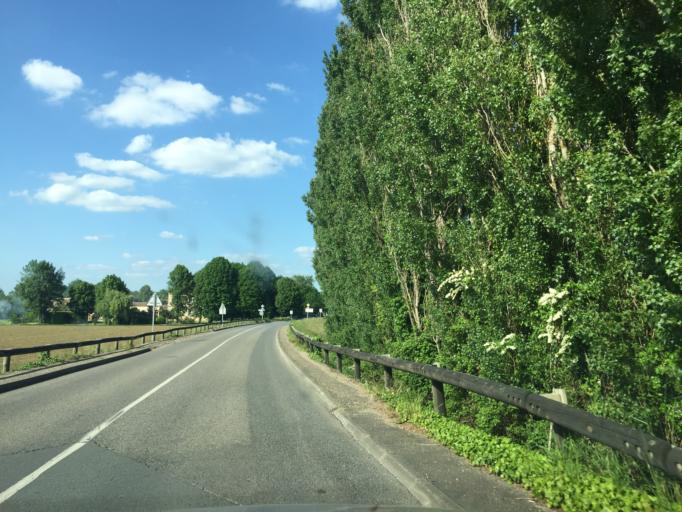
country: FR
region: Aquitaine
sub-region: Departement de la Gironde
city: Sainte-Terre
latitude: 44.8150
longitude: -0.1382
